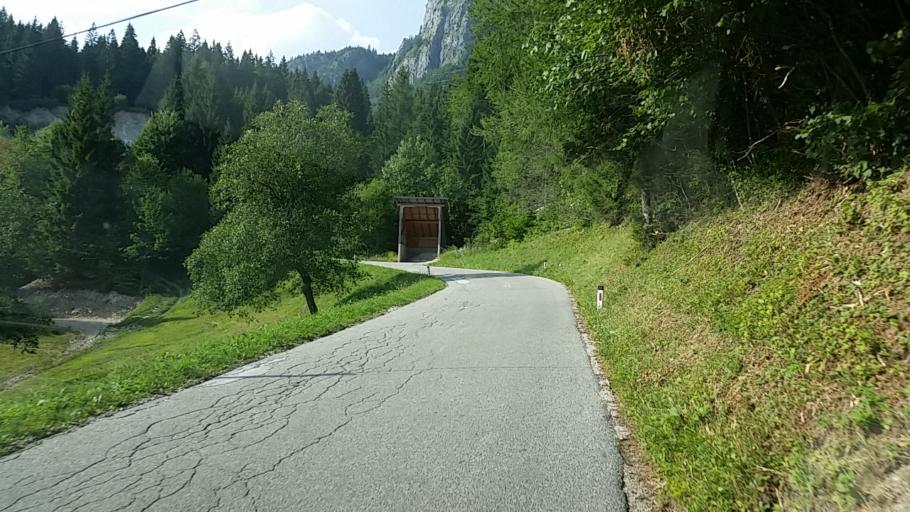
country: SI
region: Bohinj
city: Bohinjska Bistrica
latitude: 46.2269
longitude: 14.0309
